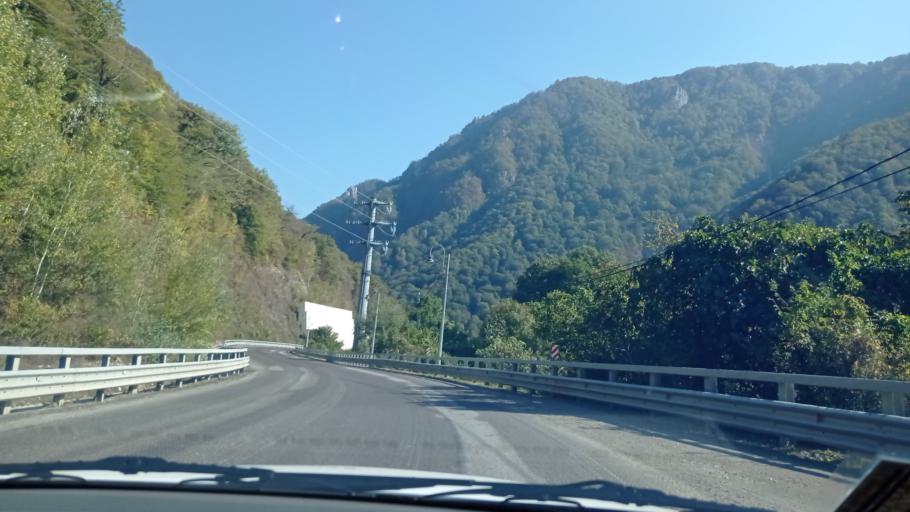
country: RU
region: Krasnodarskiy
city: Vysokoye
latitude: 43.5931
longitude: 40.0129
